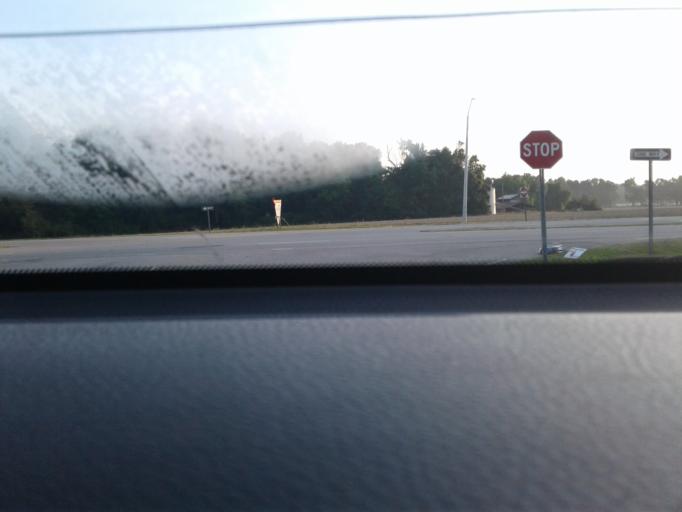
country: US
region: North Carolina
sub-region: Harnett County
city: Erwin
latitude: 35.3248
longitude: -78.6510
